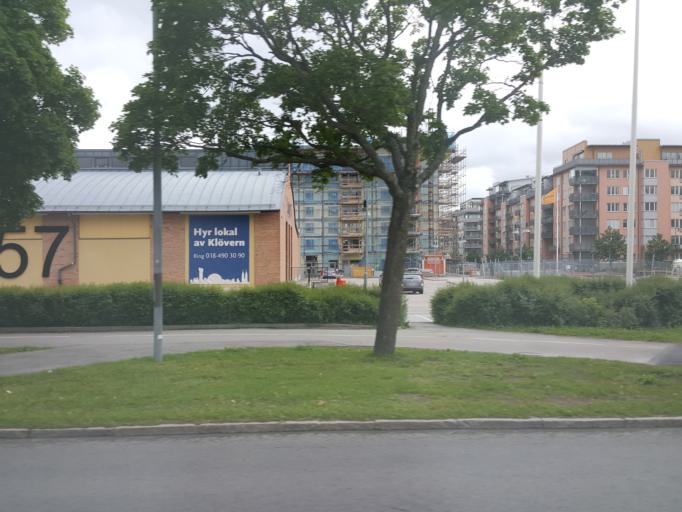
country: SE
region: Uppsala
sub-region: Uppsala Kommun
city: Uppsala
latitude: 59.8508
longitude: 17.6578
